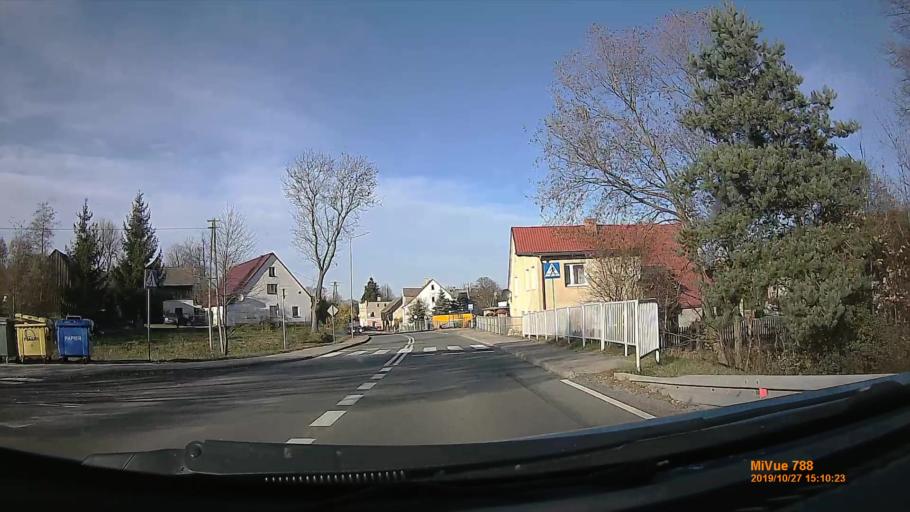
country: PL
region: Lower Silesian Voivodeship
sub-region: Powiat klodzki
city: Miedzylesie
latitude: 50.1878
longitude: 16.6713
